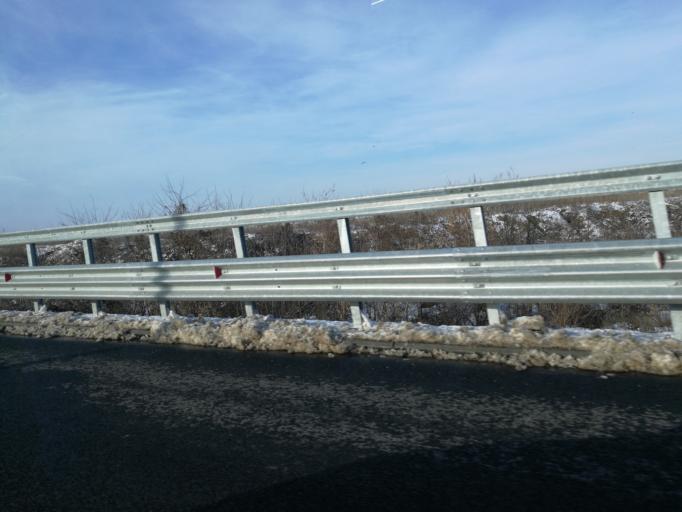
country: RO
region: Ilfov
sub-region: Comuna Fundeni-Dobroesti
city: Fundeni
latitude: 44.4787
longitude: 26.1332
